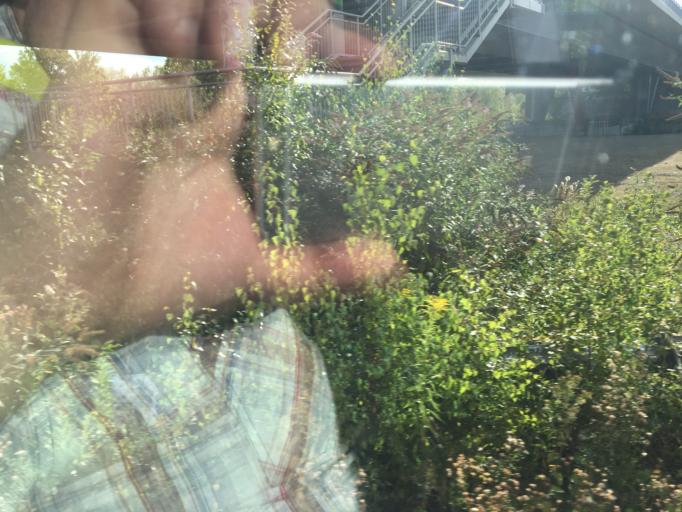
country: DE
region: North Rhine-Westphalia
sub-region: Regierungsbezirk Arnsberg
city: Dortmund
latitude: 51.4980
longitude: 7.4359
